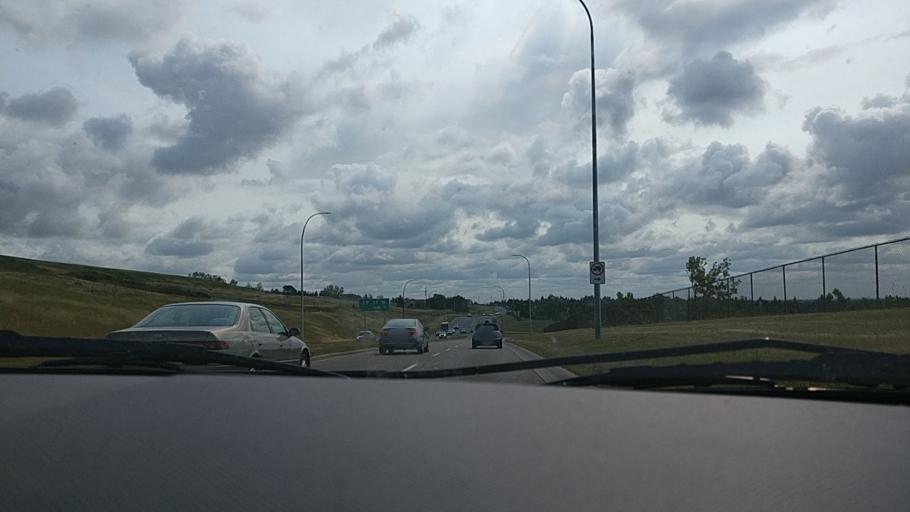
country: CA
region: Alberta
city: Calgary
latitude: 51.0934
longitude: -114.1096
